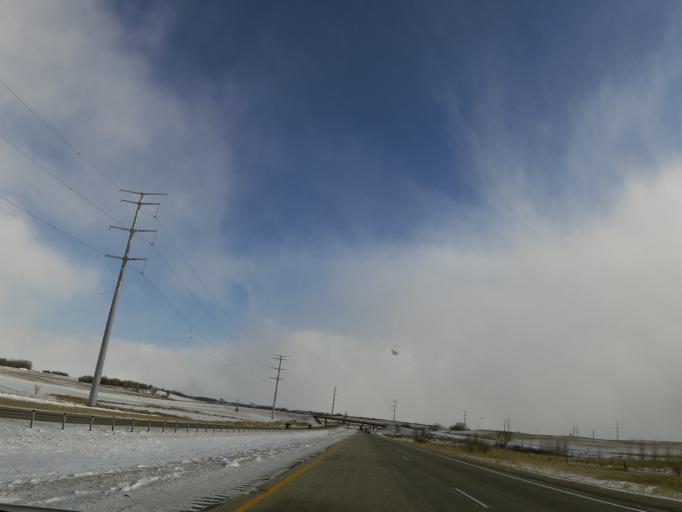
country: US
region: Minnesota
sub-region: Grant County
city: Elbow Lake
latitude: 46.1115
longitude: -95.8999
